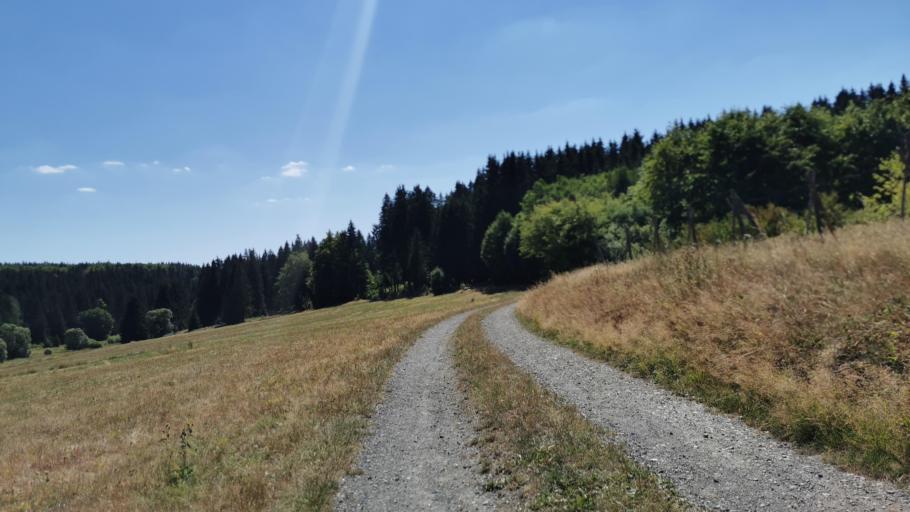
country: DE
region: Bavaria
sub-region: Upper Franconia
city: Pressig
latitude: 50.4141
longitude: 11.2928
